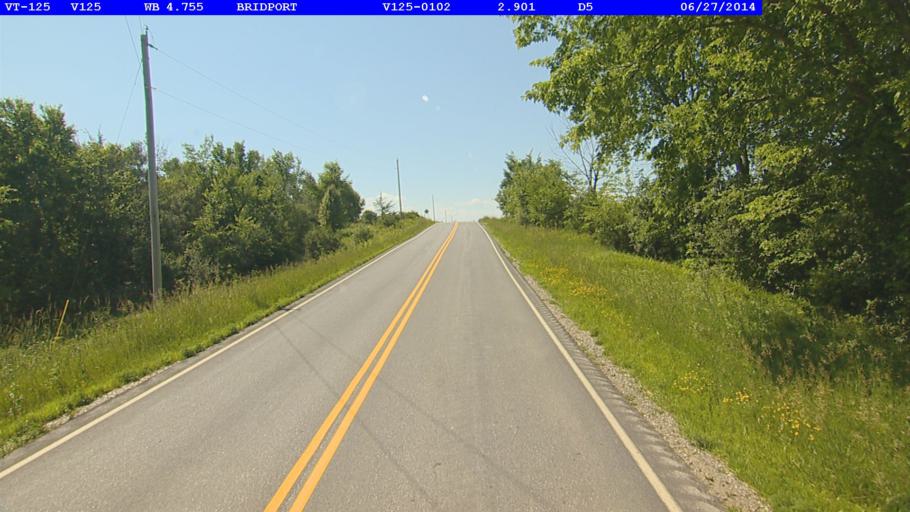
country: US
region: New York
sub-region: Essex County
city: Port Henry
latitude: 43.9975
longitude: -73.3529
